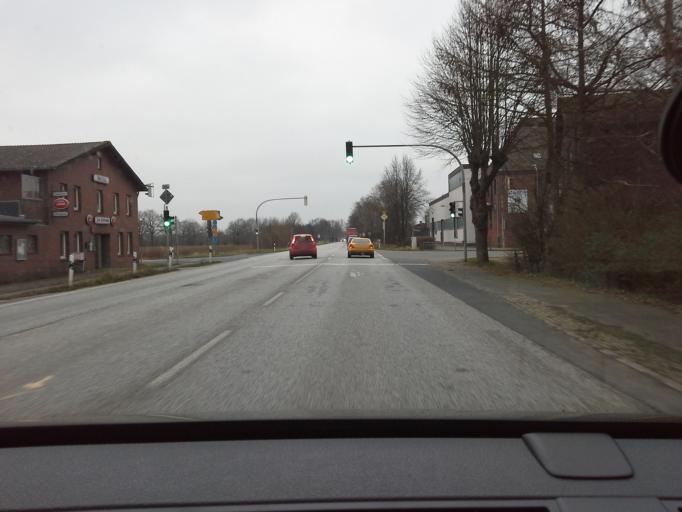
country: DE
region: Schleswig-Holstein
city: Bilsen
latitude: 53.7864
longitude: 9.8752
